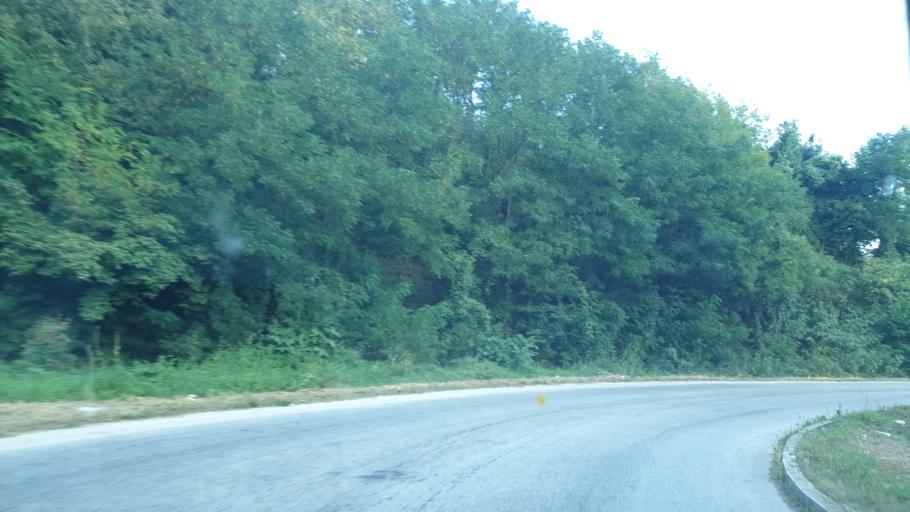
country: RS
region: Central Serbia
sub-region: Zlatiborski Okrug
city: Uzice
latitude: 43.8636
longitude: 19.8946
